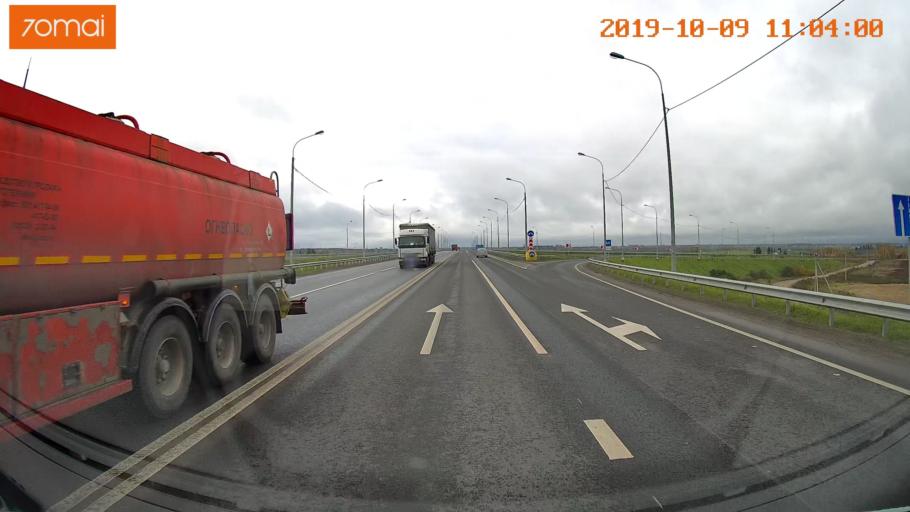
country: RU
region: Vologda
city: Vologda
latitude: 59.2164
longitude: 39.7719
